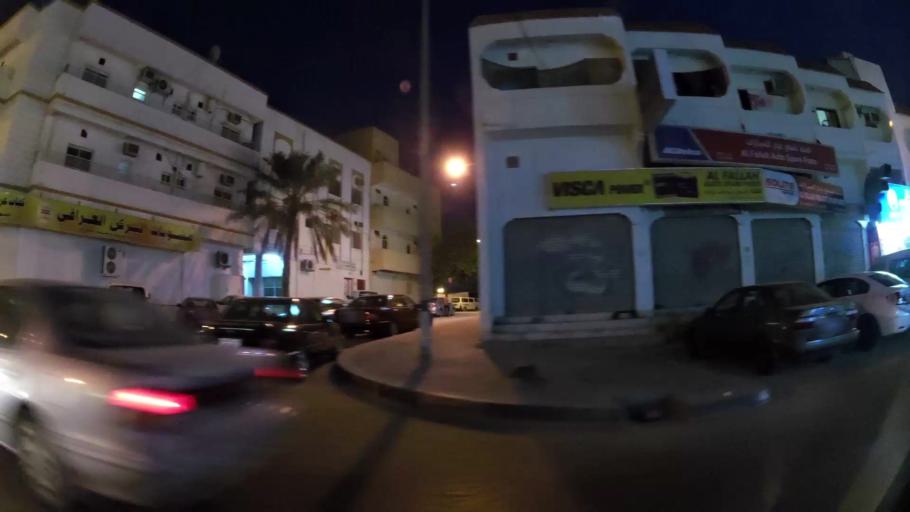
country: BH
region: Manama
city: Jidd Hafs
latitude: 26.2094
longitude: 50.5460
